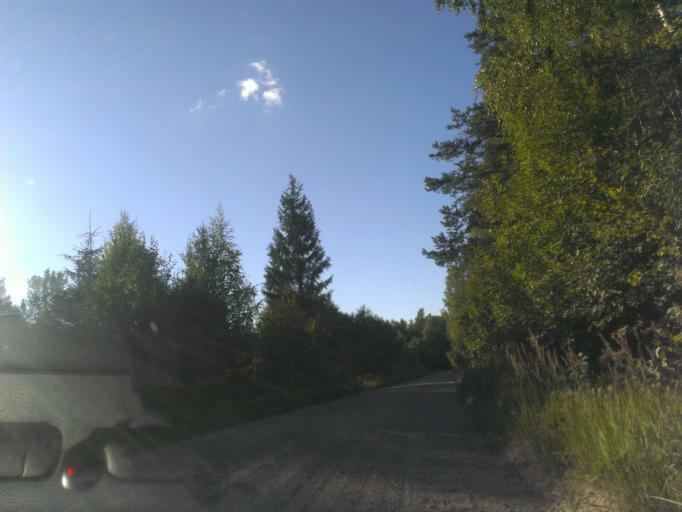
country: LV
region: Malpils
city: Malpils
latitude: 57.0979
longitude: 25.0446
